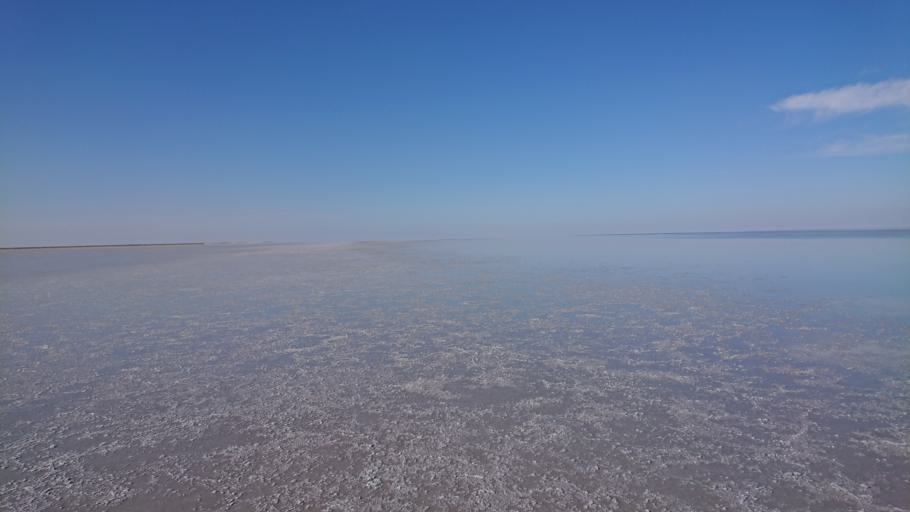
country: TR
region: Aksaray
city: Eskil
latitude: 38.4933
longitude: 33.4827
